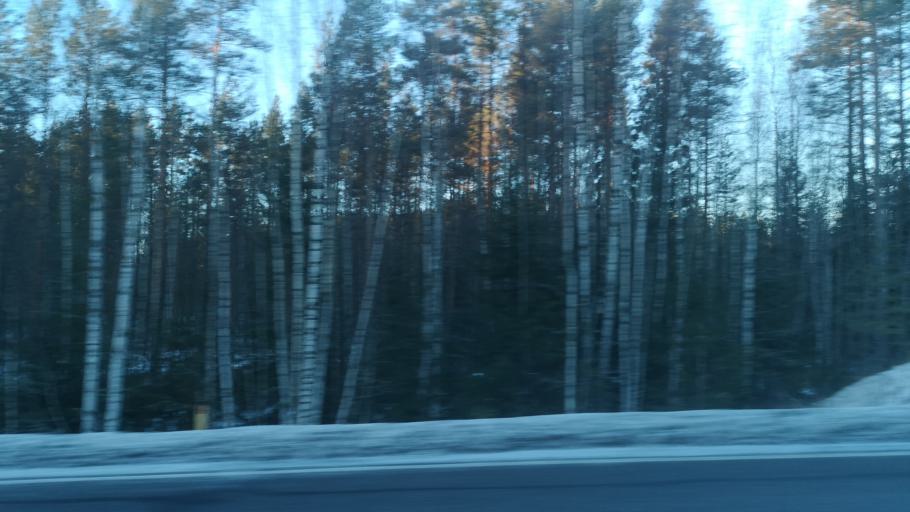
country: FI
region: Southern Savonia
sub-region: Savonlinna
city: Rantasalmi
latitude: 61.9362
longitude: 28.0994
